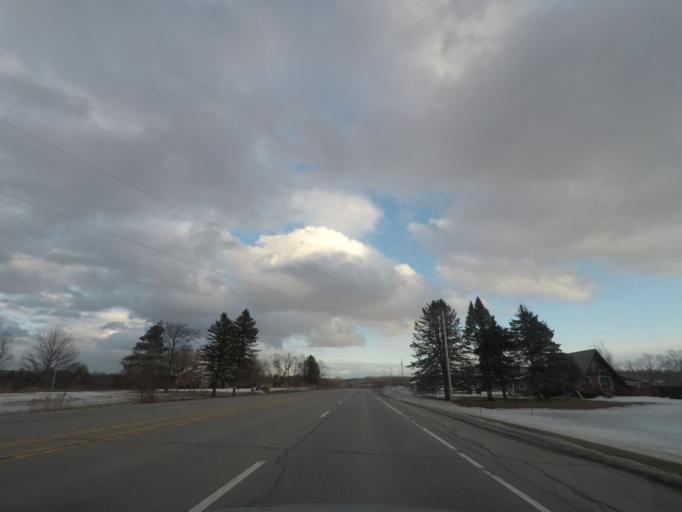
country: US
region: New York
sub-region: Herkimer County
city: Dolgeville
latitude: 43.0162
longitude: -74.7743
